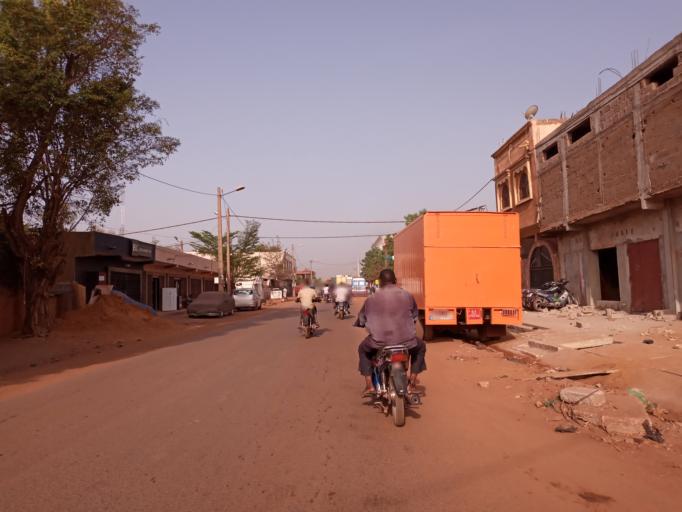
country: ML
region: Bamako
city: Bamako
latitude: 12.6639
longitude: -7.9775
